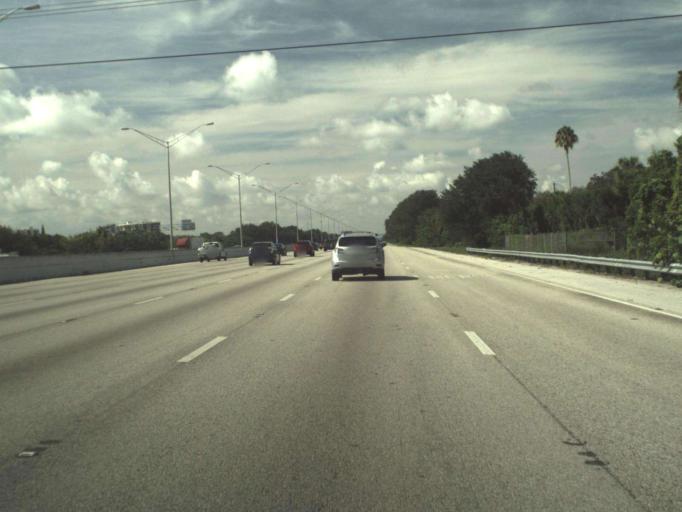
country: US
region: Florida
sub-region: Palm Beach County
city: Mangonia Park
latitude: 26.7503
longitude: -80.0904
